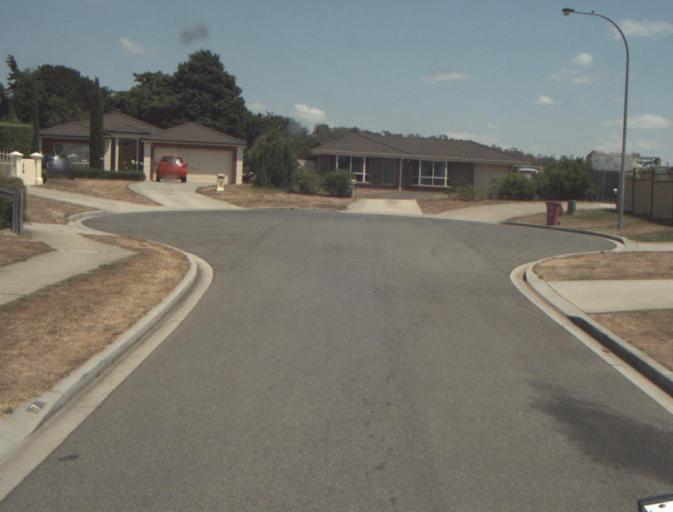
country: AU
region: Tasmania
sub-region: Launceston
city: Summerhill
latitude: -41.4891
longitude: 147.1706
